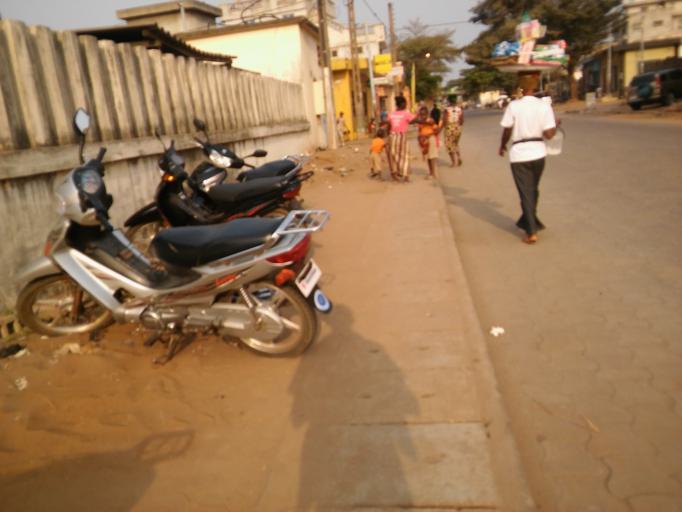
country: BJ
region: Queme
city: Porto-Novo
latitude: 6.4772
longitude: 2.6225
